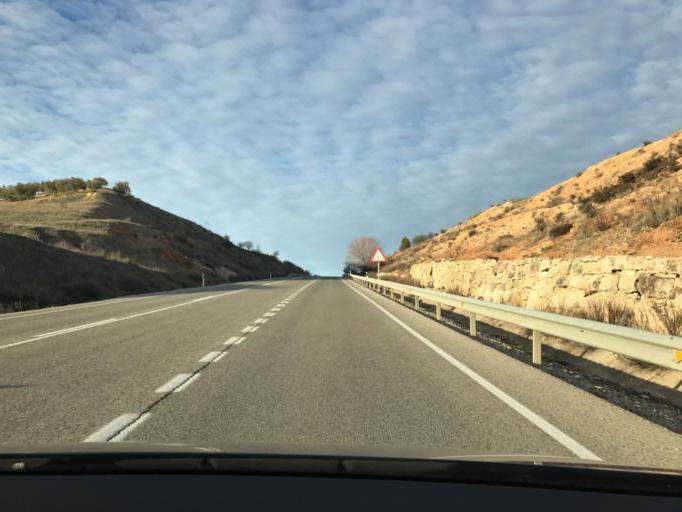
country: ES
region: Andalusia
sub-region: Provincia de Jaen
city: Guadahortuna
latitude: 37.5671
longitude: -3.4019
